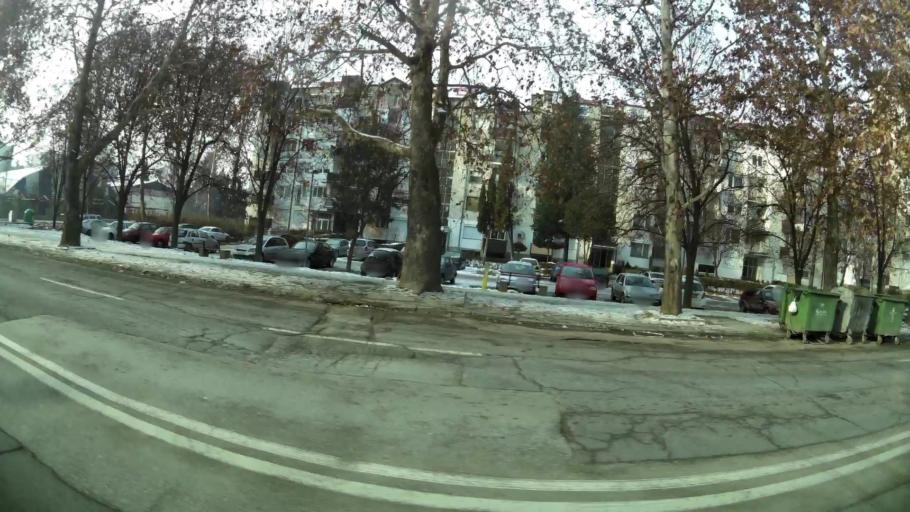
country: MK
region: Cair
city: Cair
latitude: 42.0207
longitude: 21.4344
